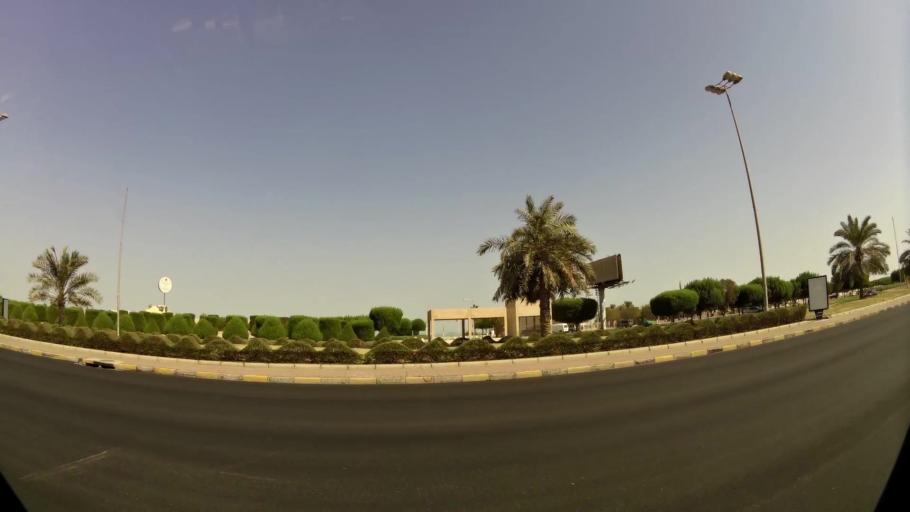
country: KW
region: Al Asimah
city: Ad Dasmah
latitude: 29.3694
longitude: 48.0115
